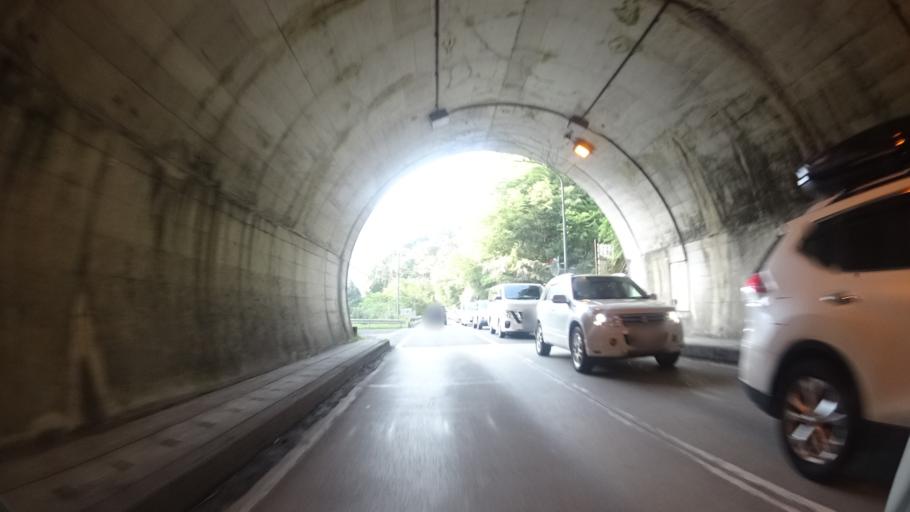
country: JP
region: Tokushima
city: Ikedacho
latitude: 33.8856
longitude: 133.8205
